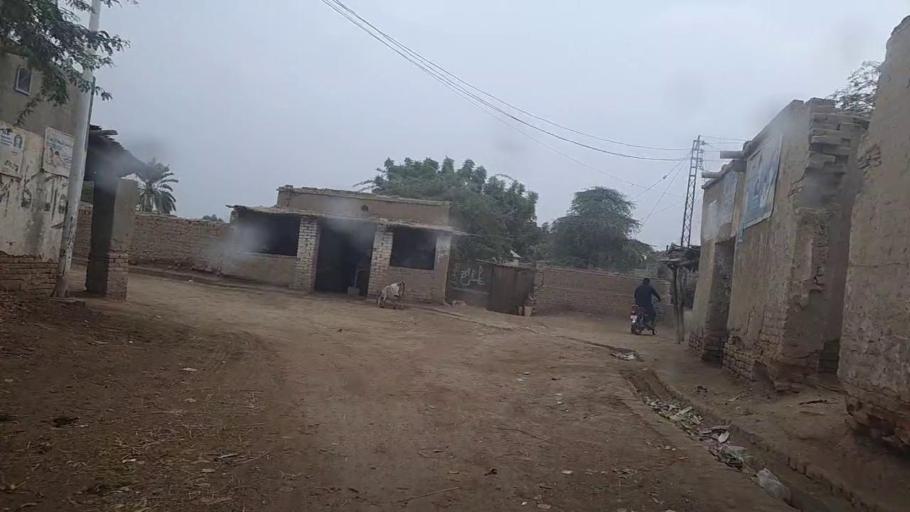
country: PK
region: Sindh
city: Gambat
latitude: 27.3599
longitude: 68.5974
